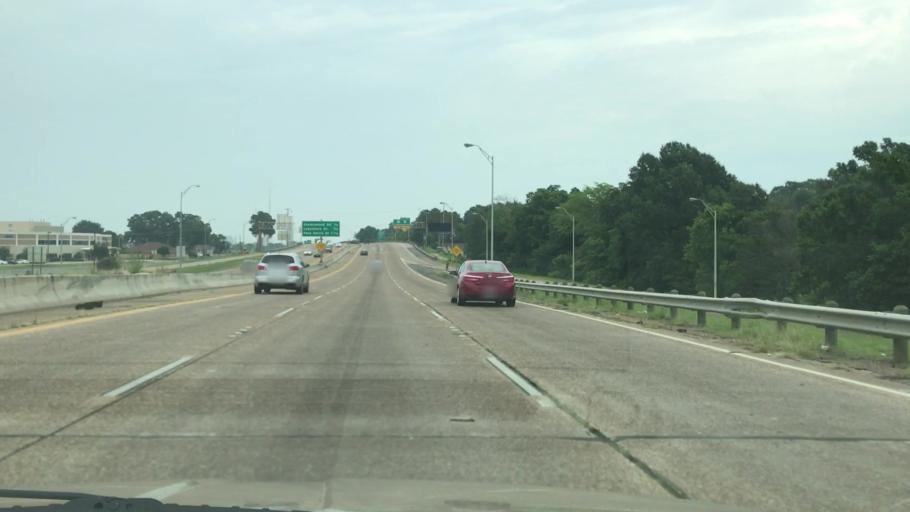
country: US
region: Louisiana
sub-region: Caddo Parish
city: Shreveport
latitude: 32.4792
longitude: -93.7795
